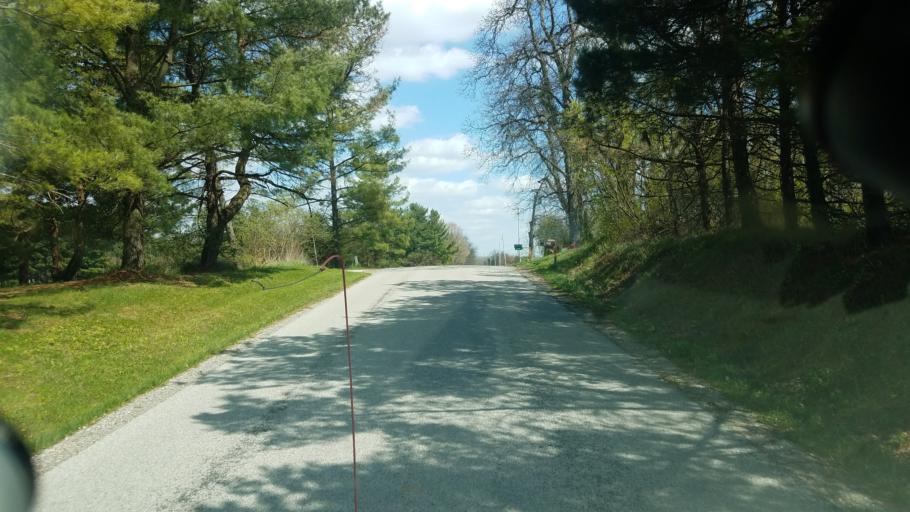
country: US
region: Ohio
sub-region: Licking County
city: Johnstown
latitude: 40.0954
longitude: -82.6502
